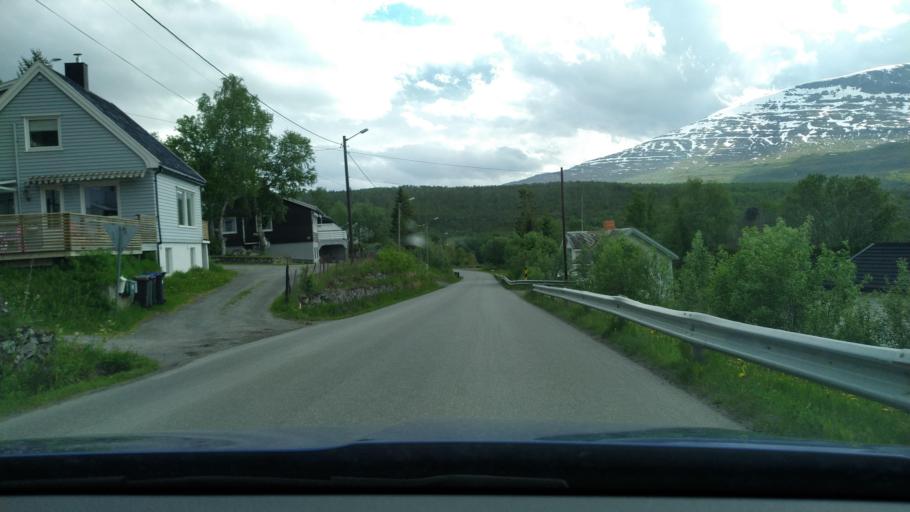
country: NO
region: Troms
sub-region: Salangen
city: Sjovegan
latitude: 68.8708
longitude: 17.8540
